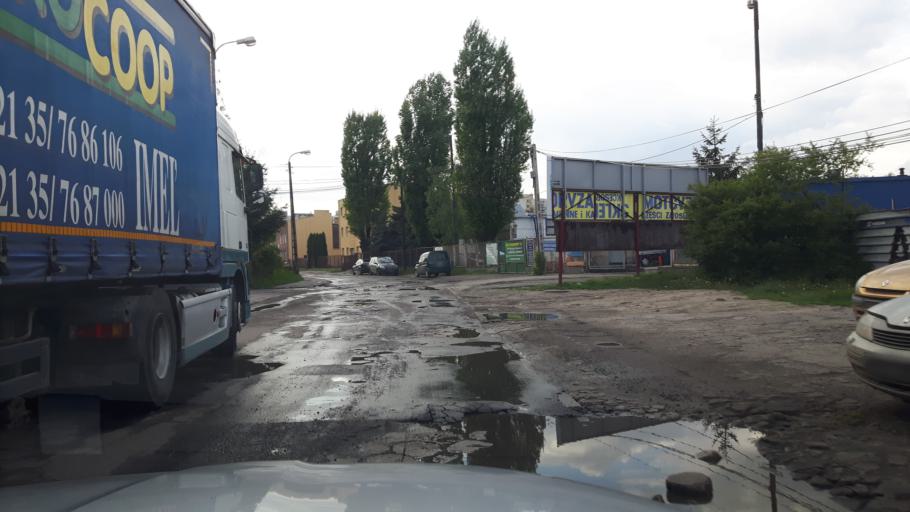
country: PL
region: Masovian Voivodeship
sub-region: Warszawa
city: Targowek
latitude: 52.2719
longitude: 21.0669
